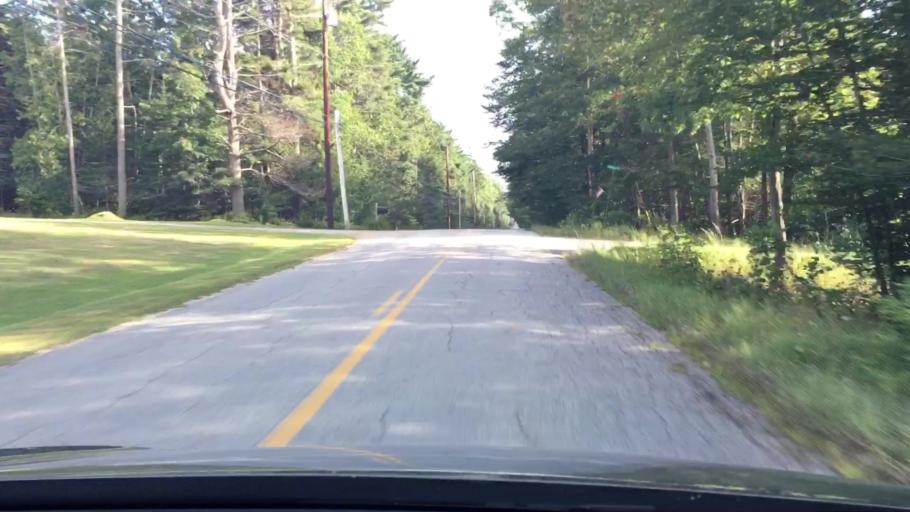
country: US
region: Maine
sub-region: Hancock County
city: Bucksport
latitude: 44.5365
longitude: -68.7941
